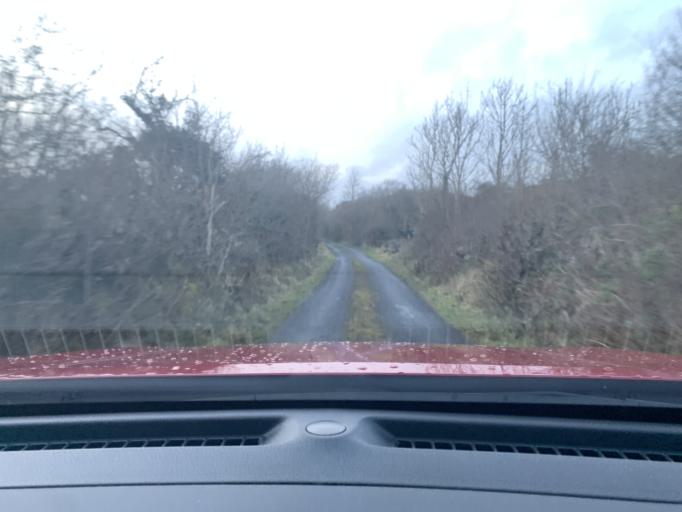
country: IE
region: Connaught
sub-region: Sligo
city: Ballymote
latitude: 53.9900
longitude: -8.4477
